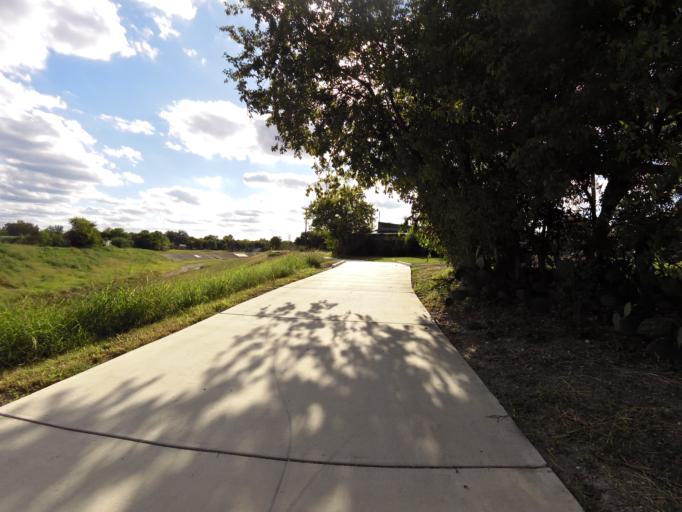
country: US
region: Texas
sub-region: Bexar County
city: San Antonio
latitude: 29.4150
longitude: -98.5166
